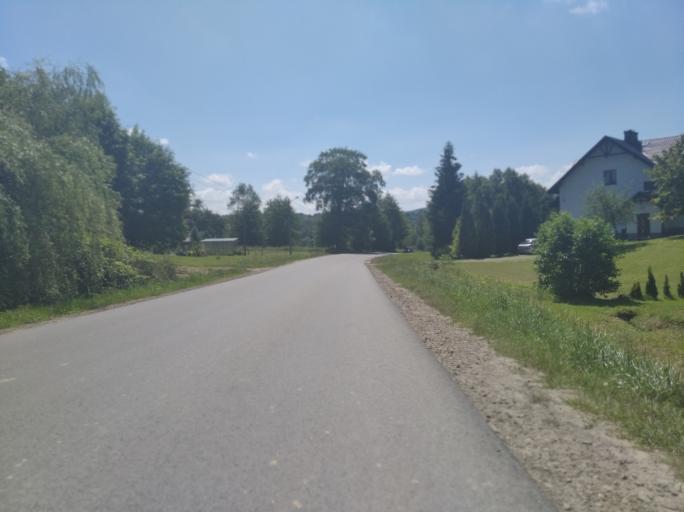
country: PL
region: Subcarpathian Voivodeship
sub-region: Powiat brzozowski
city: Jablonka
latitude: 49.6856
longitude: 22.1175
